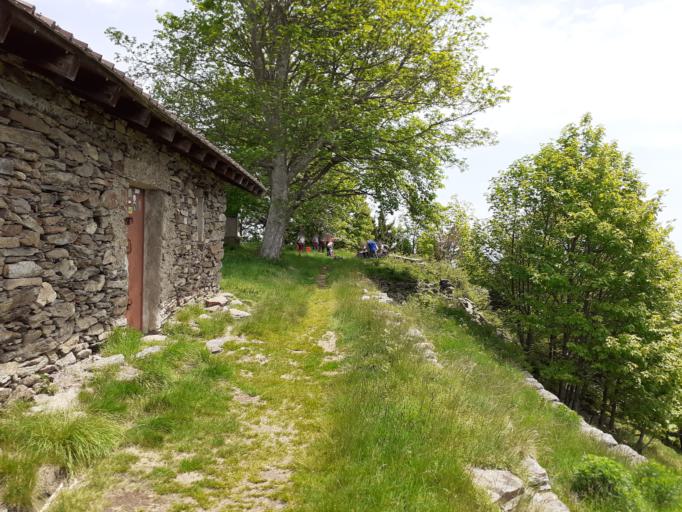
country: IT
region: Piedmont
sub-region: Provincia Verbano-Cusio-Ossola
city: Miazzina
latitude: 46.0086
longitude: 8.5344
